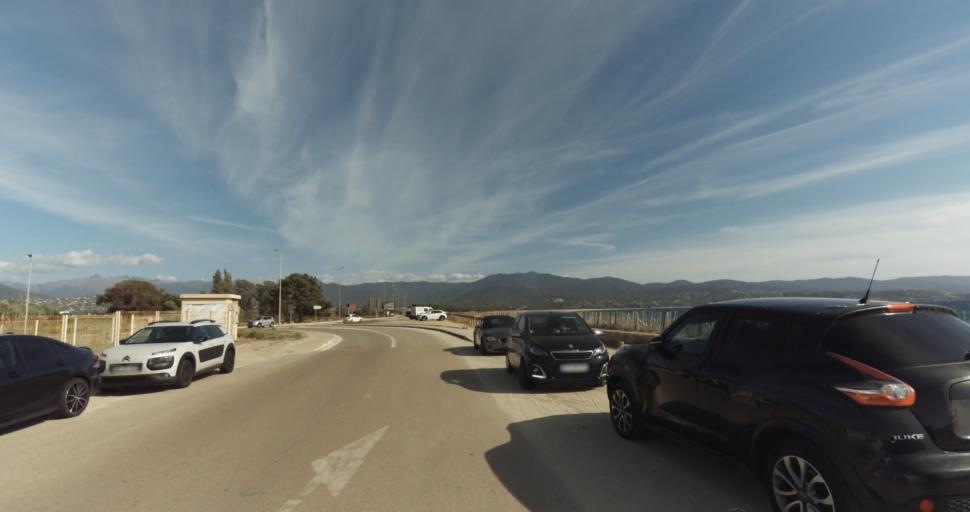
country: FR
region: Corsica
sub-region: Departement de la Corse-du-Sud
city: Ajaccio
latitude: 41.9265
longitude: 8.7778
